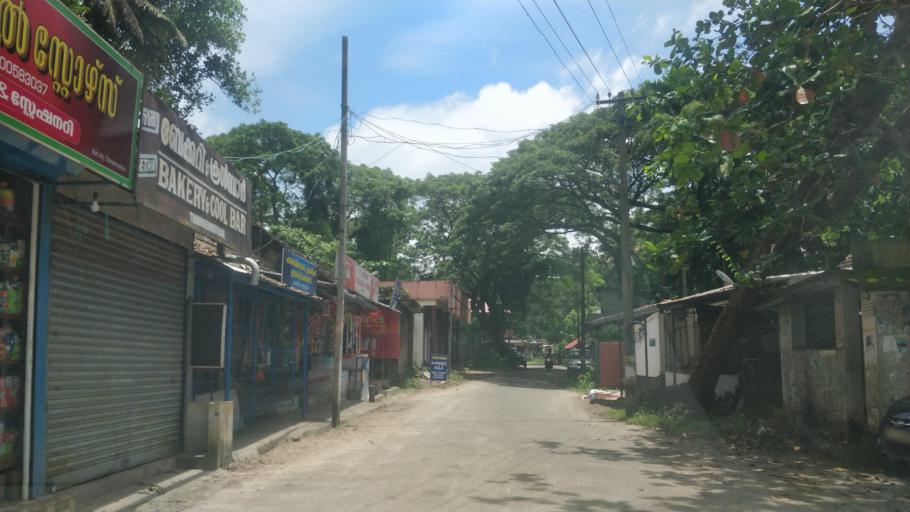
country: IN
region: Kerala
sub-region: Alappuzha
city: Shertallai
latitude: 9.6750
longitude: 76.3924
